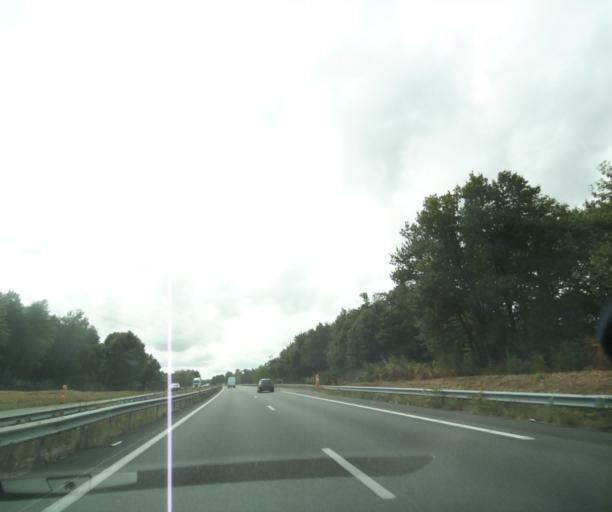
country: FR
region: Poitou-Charentes
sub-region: Departement de la Charente-Maritime
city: Saint-Genis-de-Saintonge
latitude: 45.4607
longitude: -0.6187
